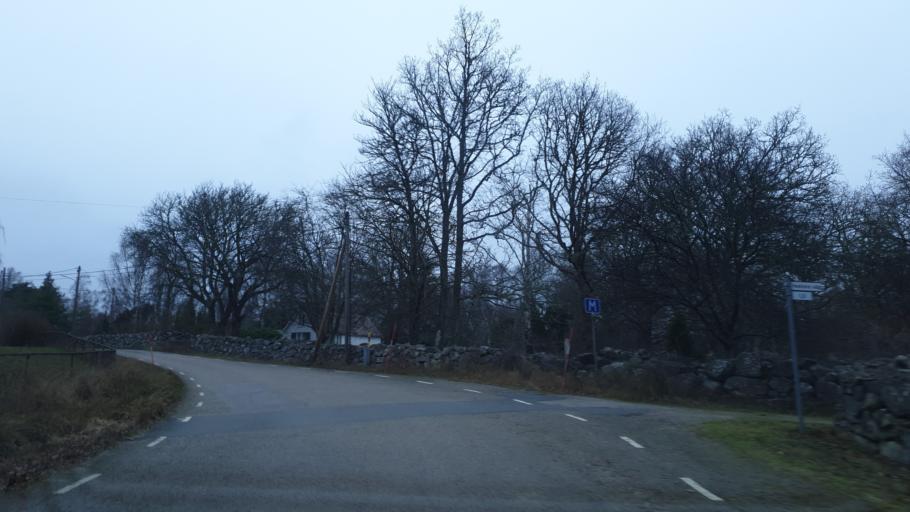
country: SE
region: Blekinge
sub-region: Karlskrona Kommun
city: Karlskrona
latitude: 56.1082
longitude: 15.6116
